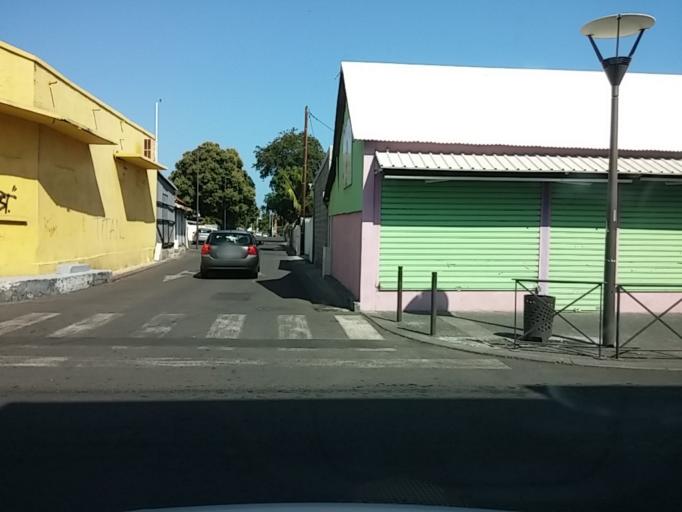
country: RE
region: Reunion
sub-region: Reunion
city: Le Port
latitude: -20.9387
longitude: 55.2940
